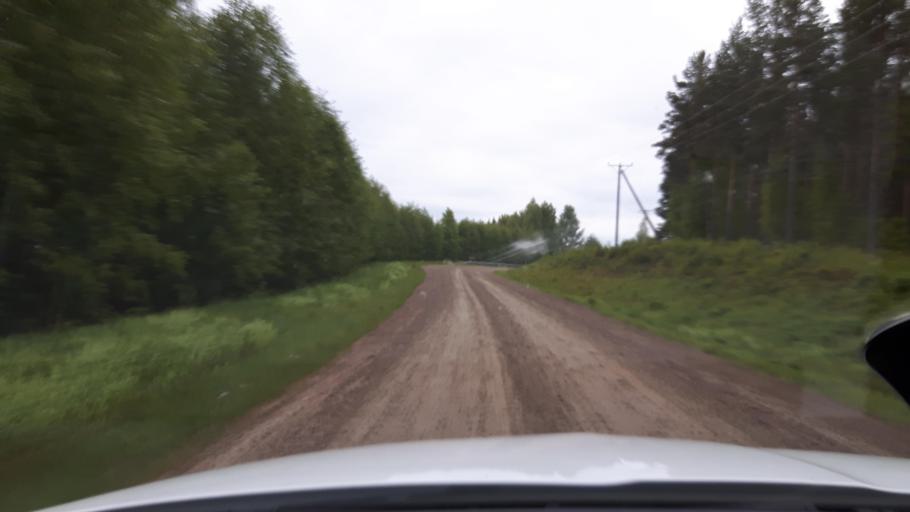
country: SE
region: Vaesternorrland
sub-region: Ange Kommun
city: Ange
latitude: 62.1560
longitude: 15.6628
